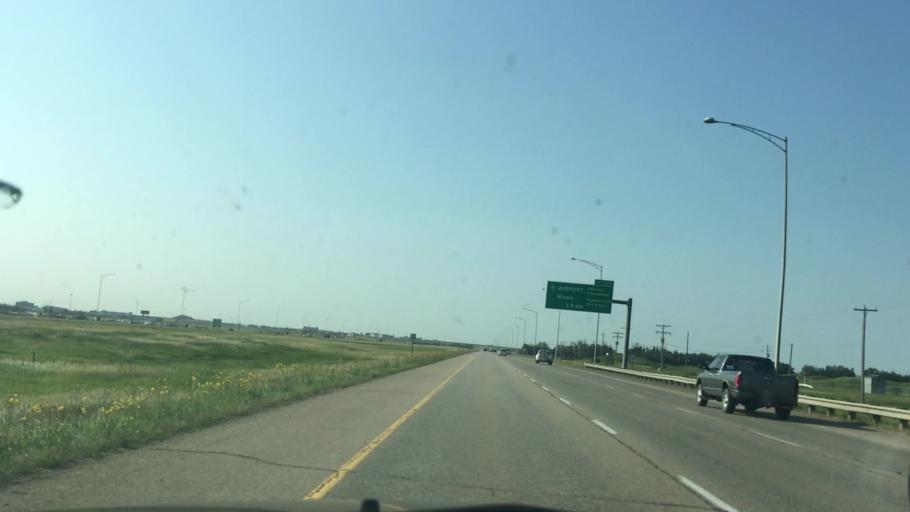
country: CA
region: Alberta
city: Leduc
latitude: 53.3309
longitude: -113.5499
